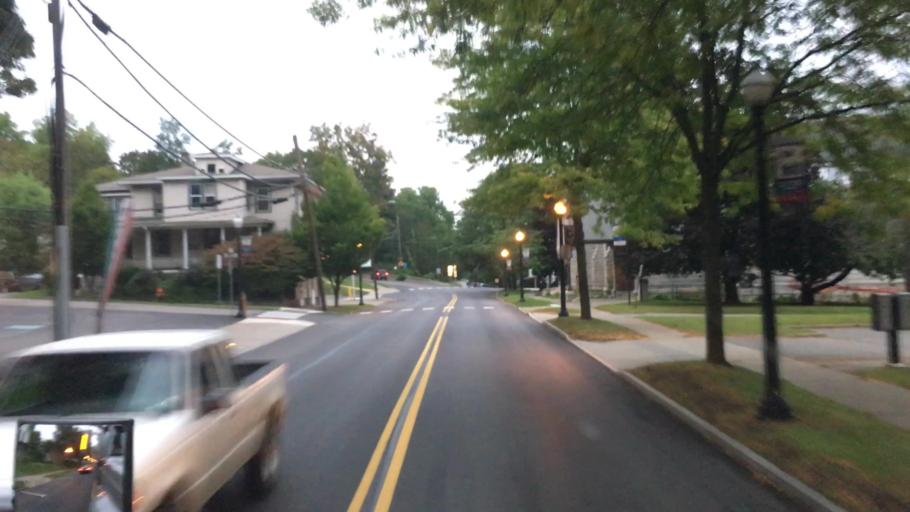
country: US
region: Pennsylvania
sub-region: Bradford County
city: Towanda
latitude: 41.7703
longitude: -76.4432
